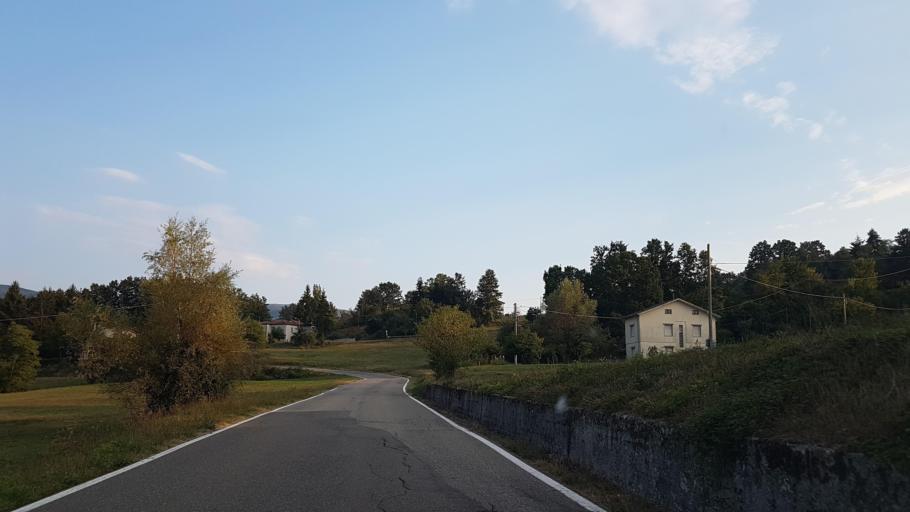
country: IT
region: Emilia-Romagna
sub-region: Provincia di Parma
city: Albareto
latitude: 44.4746
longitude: 9.7081
